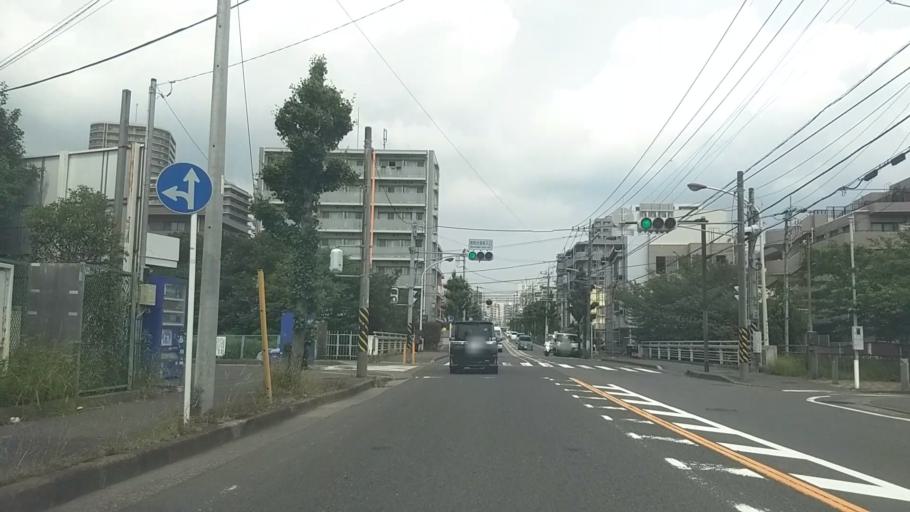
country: JP
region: Kanagawa
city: Fujisawa
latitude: 35.3966
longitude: 139.4605
